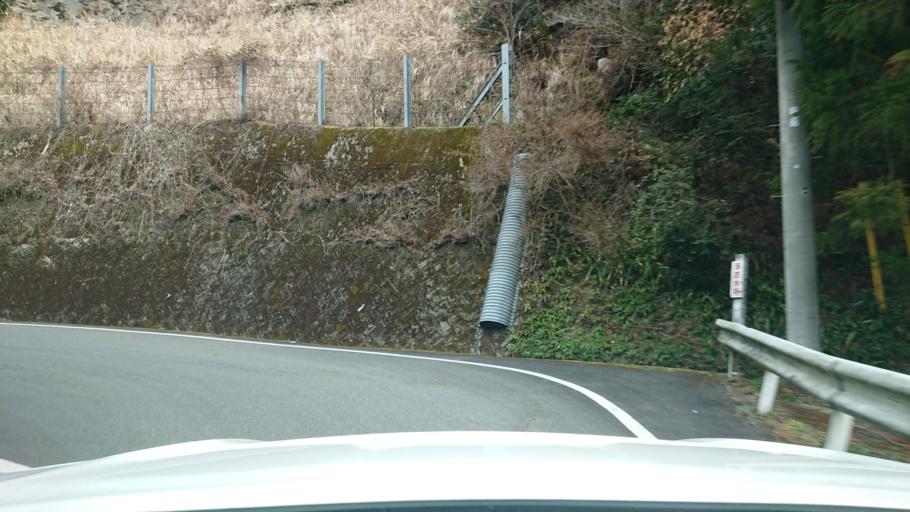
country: JP
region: Tokushima
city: Ishii
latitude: 33.9066
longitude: 134.3960
